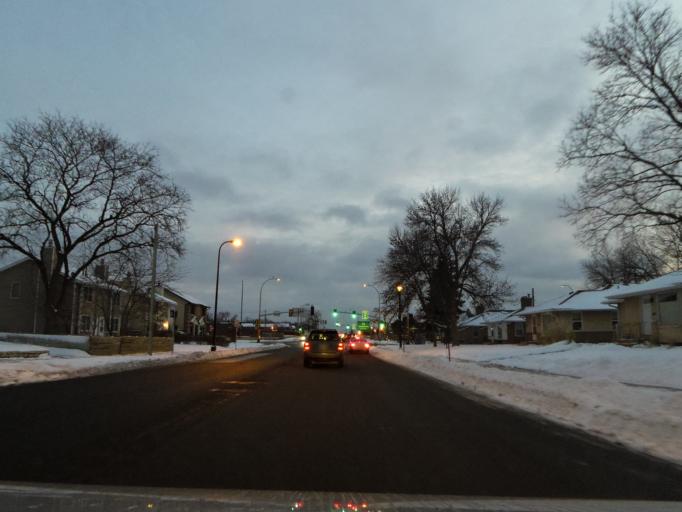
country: US
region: Minnesota
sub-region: Hennepin County
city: Richfield
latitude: 44.8920
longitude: -93.3087
